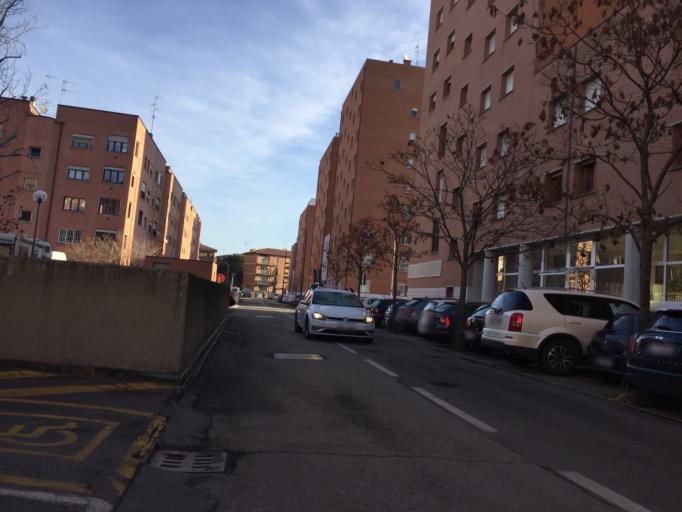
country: IT
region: Emilia-Romagna
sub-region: Provincia di Bologna
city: Casalecchio di Reno
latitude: 44.4940
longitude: 11.2928
